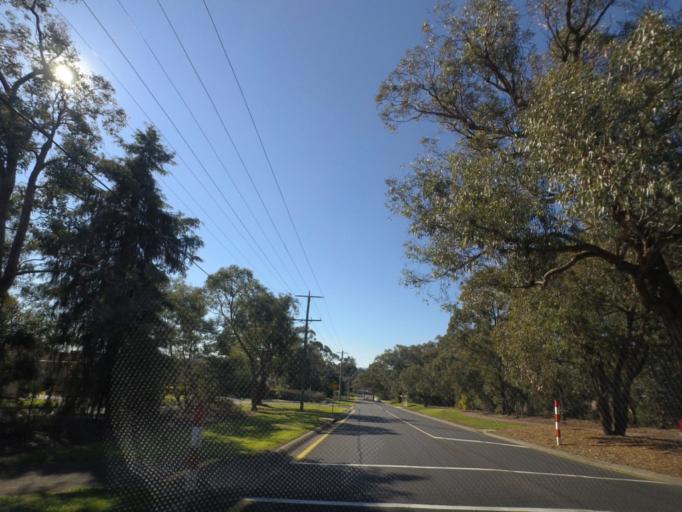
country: AU
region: Victoria
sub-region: Maroondah
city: Croydon Hills
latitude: -37.7760
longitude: 145.2753
